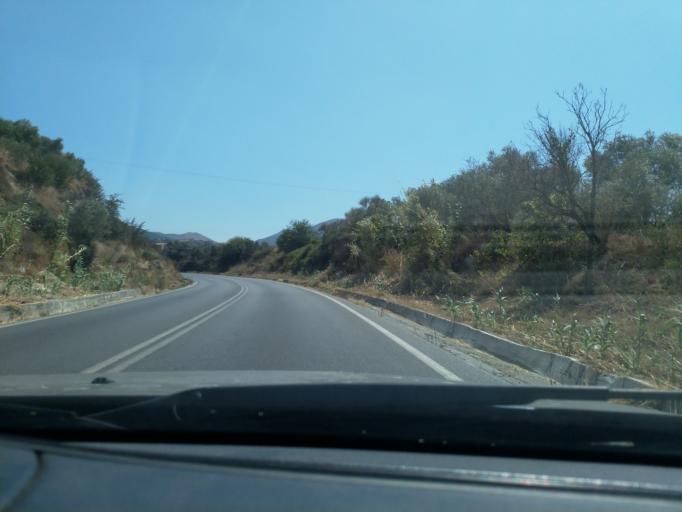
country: GR
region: Crete
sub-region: Nomos Rethymnis
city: Atsipopoulon
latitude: 35.2282
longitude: 24.4756
